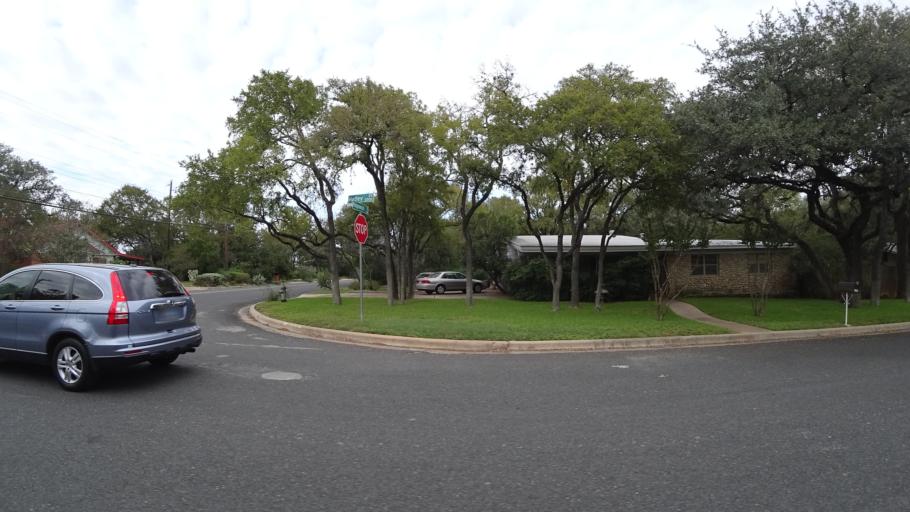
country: US
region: Texas
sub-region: Travis County
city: Rollingwood
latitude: 30.2806
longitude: -97.7888
